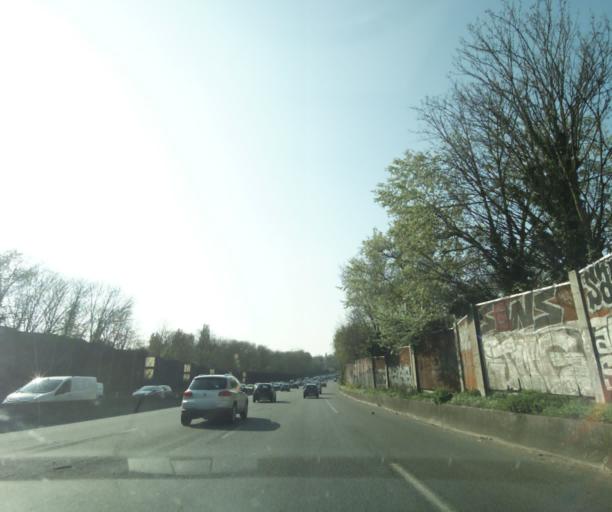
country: FR
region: Ile-de-France
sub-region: Departement de l'Essonne
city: Morsang-sur-Orge
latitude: 48.6685
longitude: 2.3535
